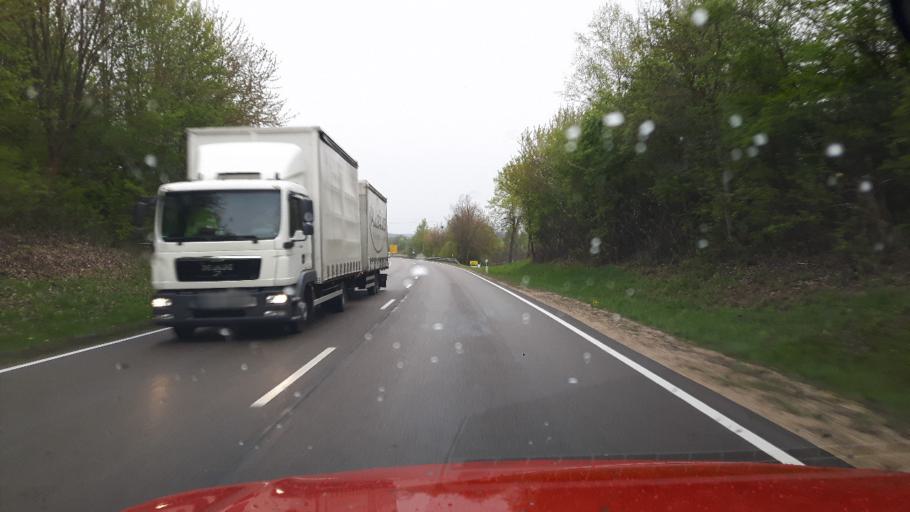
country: DE
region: Bavaria
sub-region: Regierungsbezirk Mittelfranken
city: Weissenburg in Bayern
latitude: 49.0456
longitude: 10.9763
